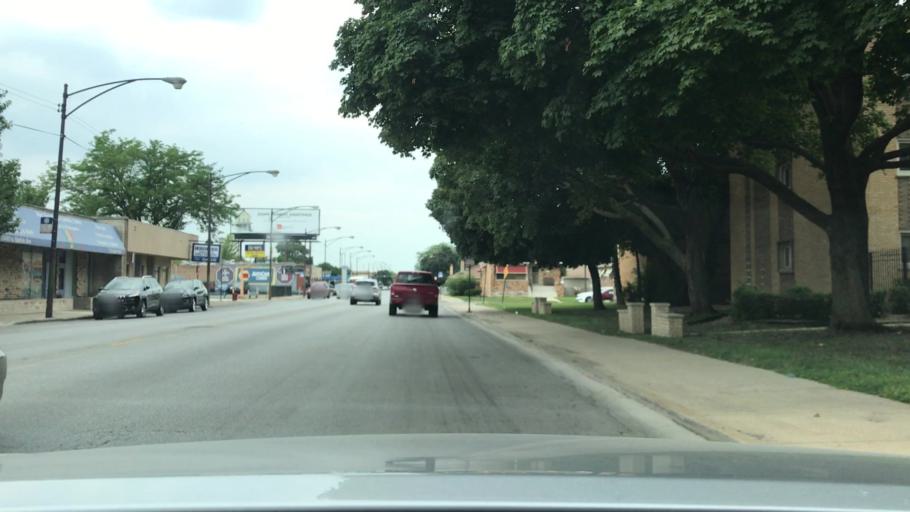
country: US
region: Illinois
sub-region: Cook County
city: Evergreen Park
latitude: 41.7391
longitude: -87.7020
